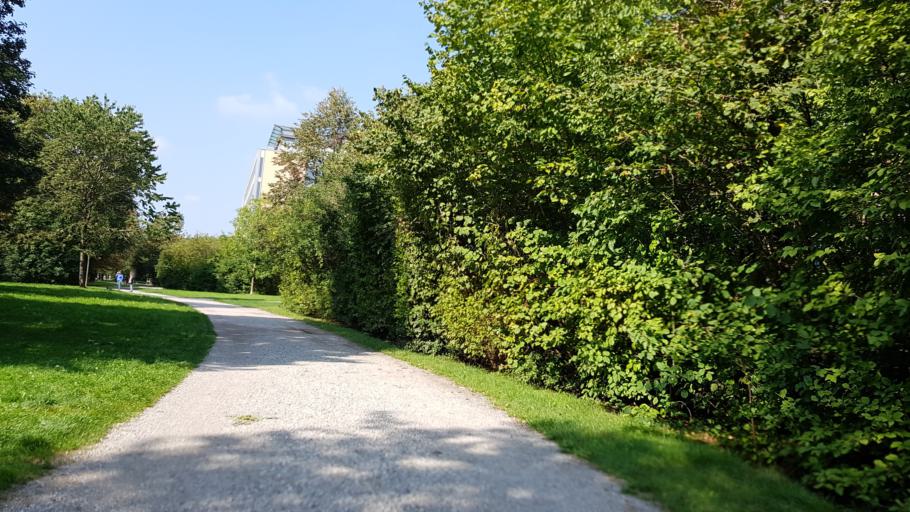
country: DE
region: Bavaria
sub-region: Upper Bavaria
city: Munich
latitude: 48.1713
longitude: 11.5353
